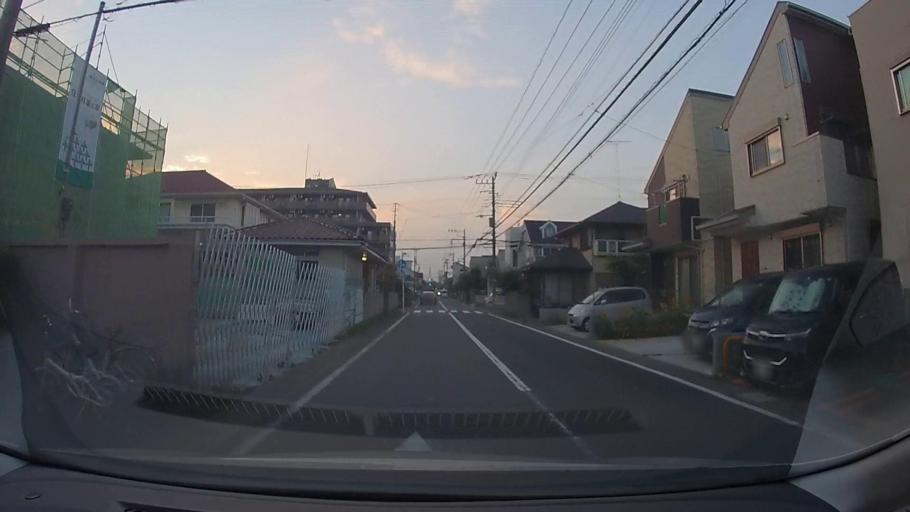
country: JP
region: Kanagawa
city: Minami-rinkan
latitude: 35.4957
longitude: 139.4436
